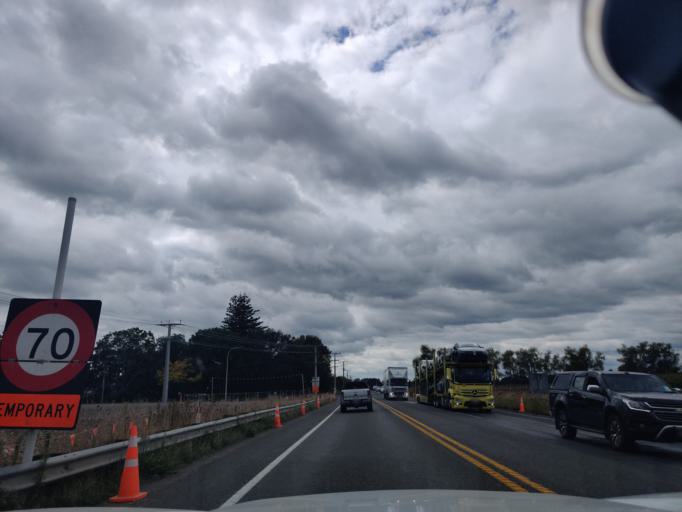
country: NZ
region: Wellington
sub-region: Kapiti Coast District
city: Otaki
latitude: -40.7479
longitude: 175.1670
